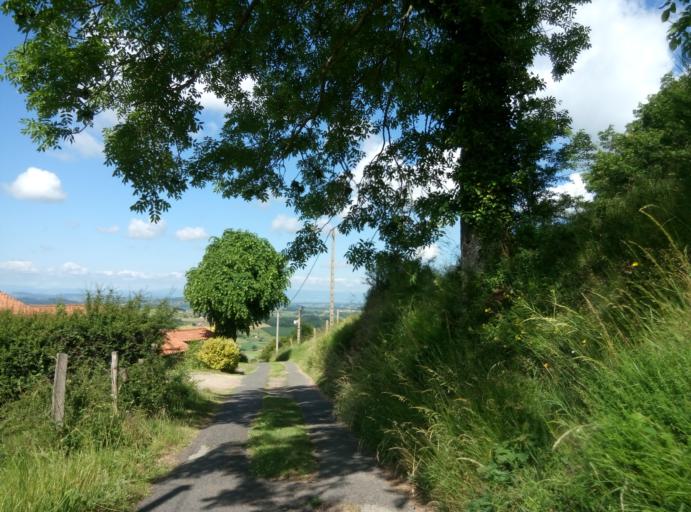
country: FR
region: Rhone-Alpes
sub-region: Departement du Rhone
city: Cublize
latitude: 45.9917
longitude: 4.3965
